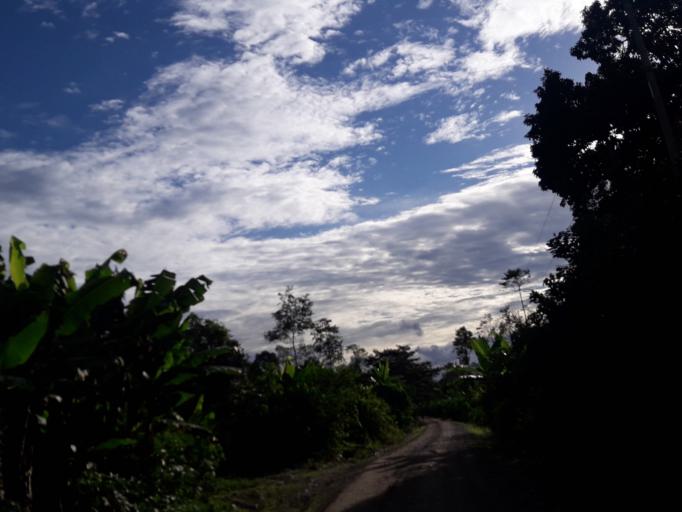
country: EC
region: Orellana
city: Boca Suno
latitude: -0.8834
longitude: -77.2922
